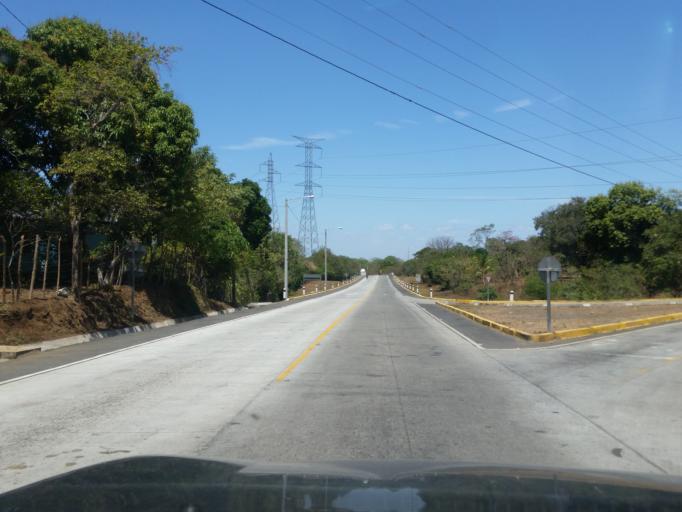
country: NI
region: Masaya
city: Masaya
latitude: 11.9754
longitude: -86.0744
